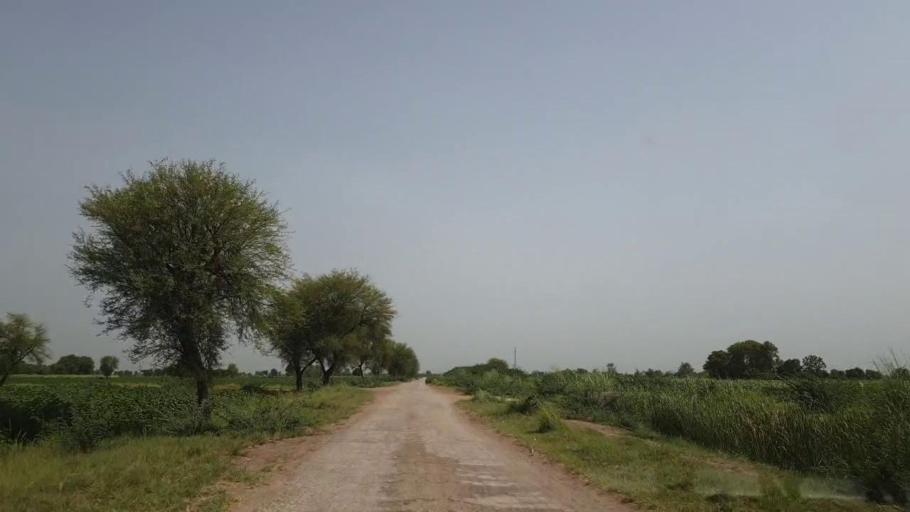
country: PK
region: Sindh
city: Sakrand
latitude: 26.1344
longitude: 68.3642
